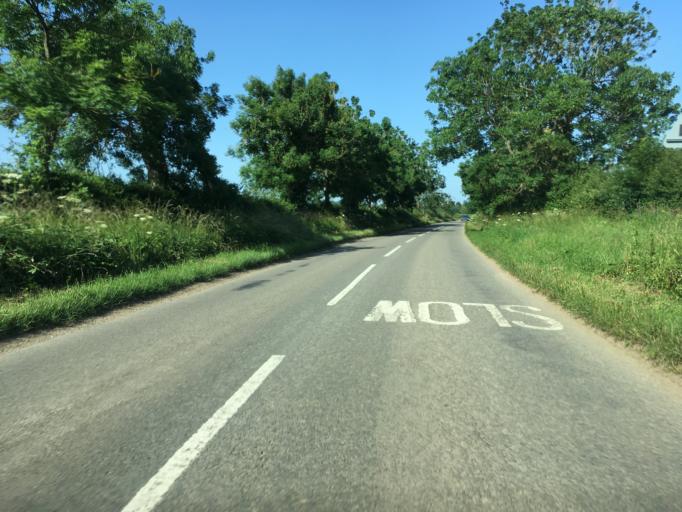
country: GB
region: England
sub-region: Buckinghamshire
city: Steeple Claydon
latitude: 51.9356
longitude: -0.9998
